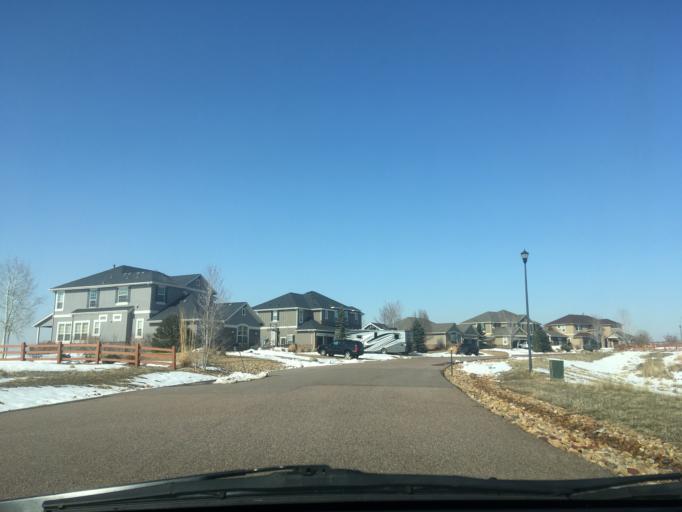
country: US
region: Colorado
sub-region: Boulder County
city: Lafayette
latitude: 39.9710
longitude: -105.0553
